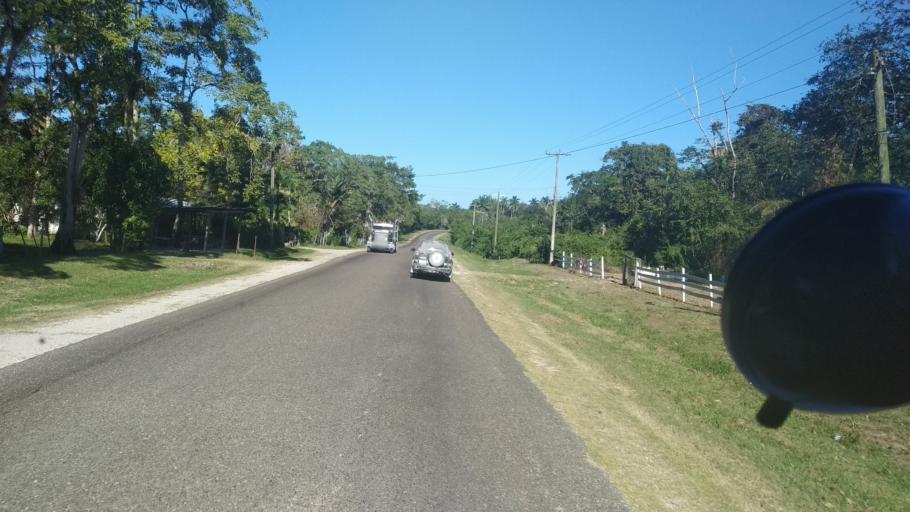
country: BZ
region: Cayo
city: San Ignacio
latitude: 17.1881
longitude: -88.9946
